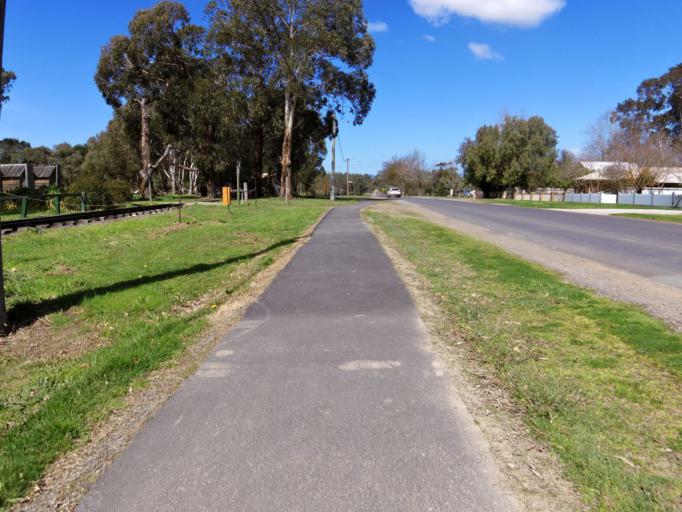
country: AU
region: Victoria
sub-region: Murrindindi
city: Alexandra
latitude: -37.1851
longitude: 145.7139
